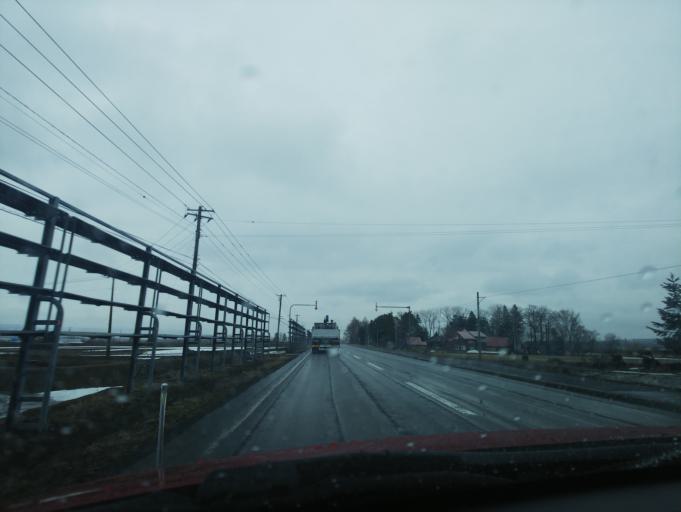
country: JP
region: Hokkaido
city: Nayoro
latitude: 44.2179
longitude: 142.3949
